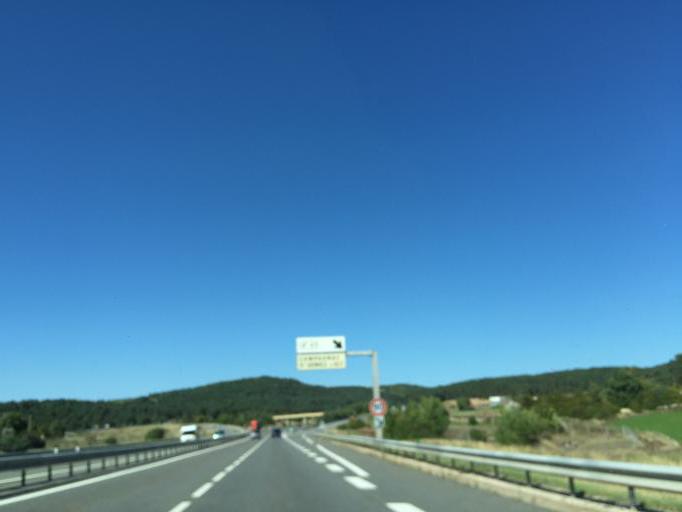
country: FR
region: Midi-Pyrenees
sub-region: Departement de l'Aveyron
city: Severac-le-Chateau
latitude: 44.3805
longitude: 3.1163
